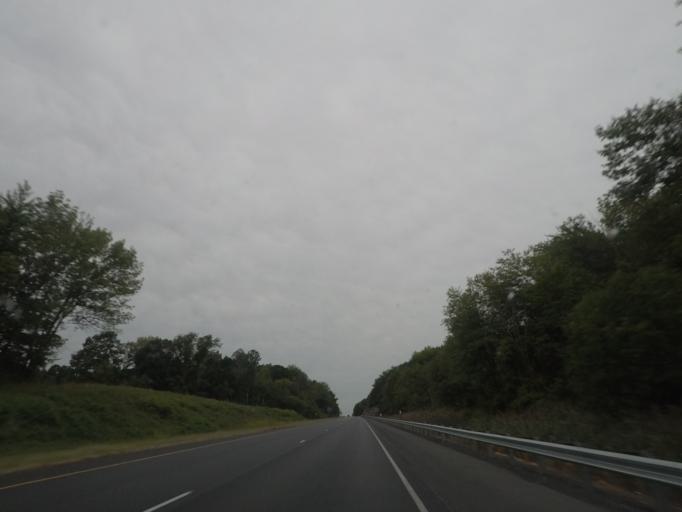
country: US
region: New York
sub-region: Columbia County
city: Niverville
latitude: 42.4839
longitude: -73.6516
